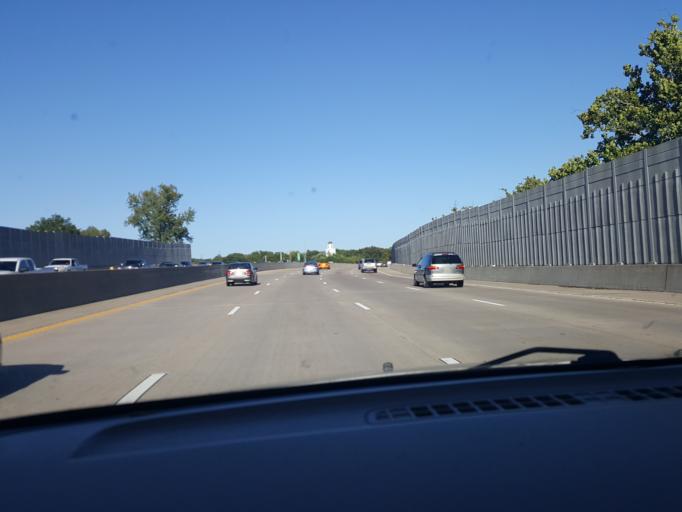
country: US
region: Missouri
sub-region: Saint Louis County
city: Frontenac
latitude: 38.6361
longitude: -90.3971
